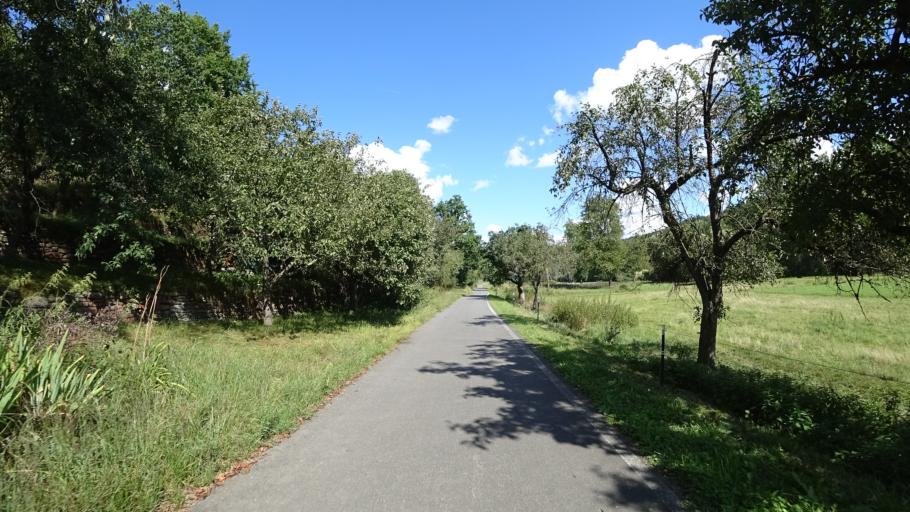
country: DE
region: Bavaria
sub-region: Regierungsbezirk Unterfranken
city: Eichenbuhl
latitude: 49.7087
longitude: 9.2990
